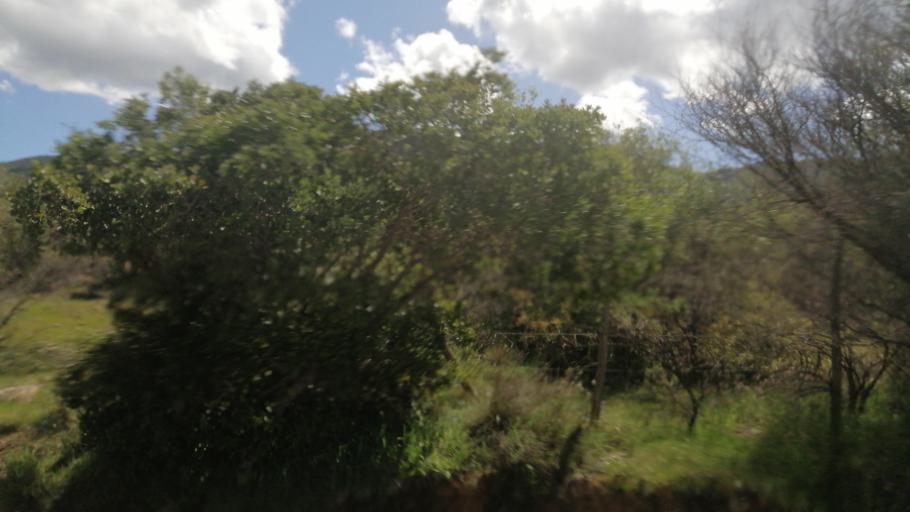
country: CL
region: Valparaiso
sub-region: Provincia de Marga Marga
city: Limache
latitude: -33.1848
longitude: -71.1887
